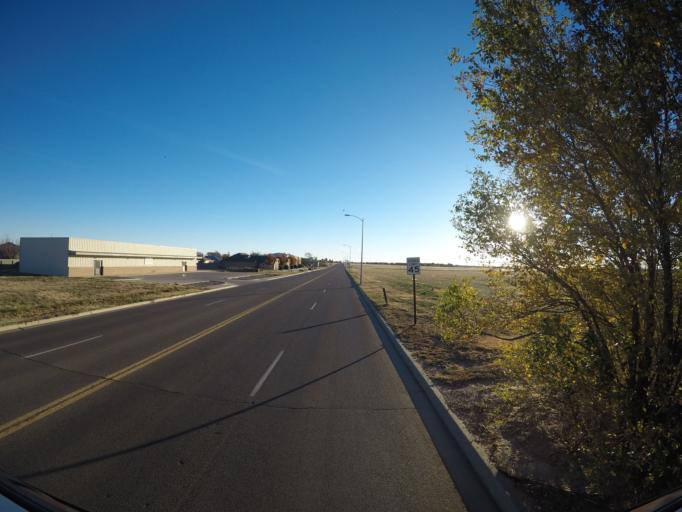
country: US
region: New Mexico
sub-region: Curry County
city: Clovis
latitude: 34.4048
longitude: -103.1780
